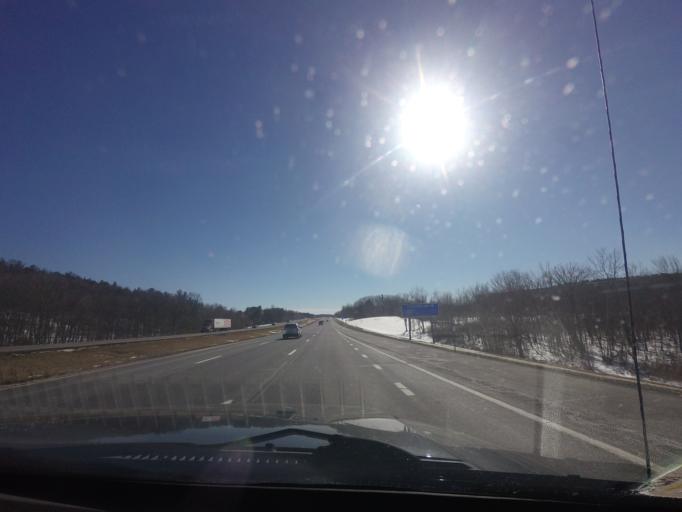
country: US
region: New York
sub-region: Rensselaer County
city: East Greenbush
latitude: 42.5738
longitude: -73.6792
